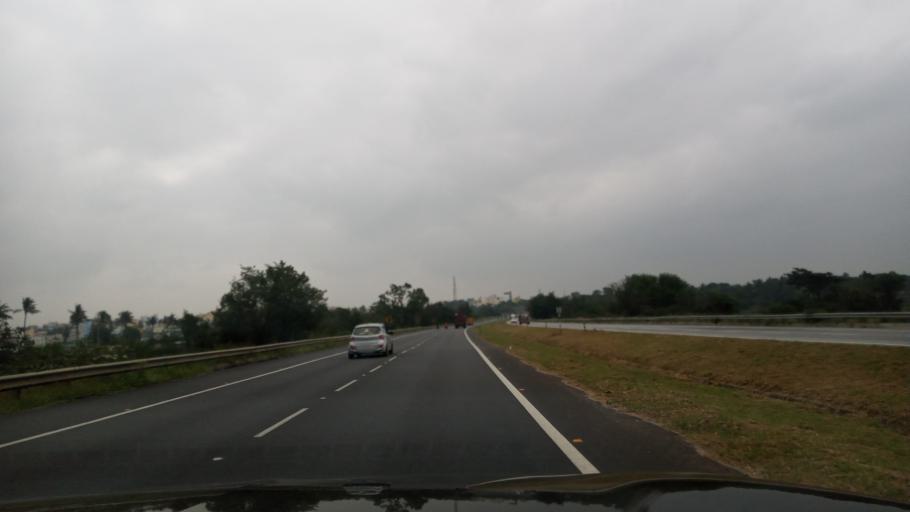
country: IN
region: Karnataka
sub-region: Bangalore Rural
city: Nelamangala
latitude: 13.0201
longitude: 77.4760
